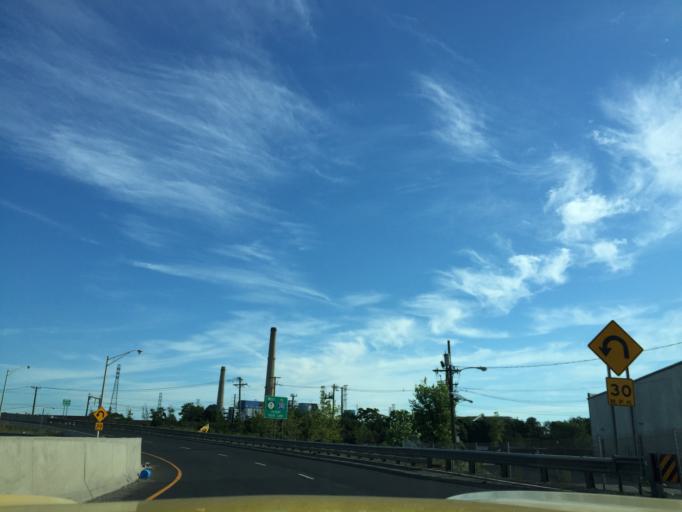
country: US
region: New Jersey
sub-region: Hudson County
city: Jersey City
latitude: 40.7396
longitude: -74.0735
